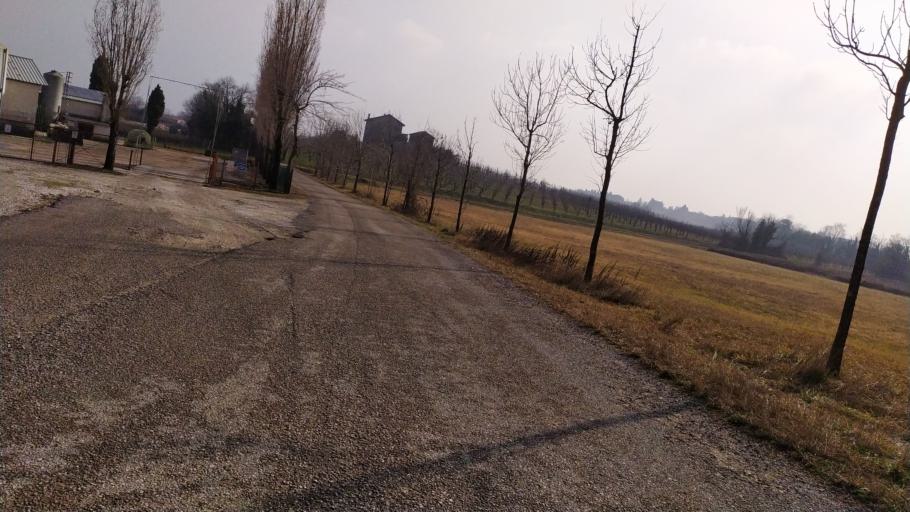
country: IT
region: Veneto
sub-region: Provincia di Treviso
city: Colle Umberto
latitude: 45.9342
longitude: 12.3494
